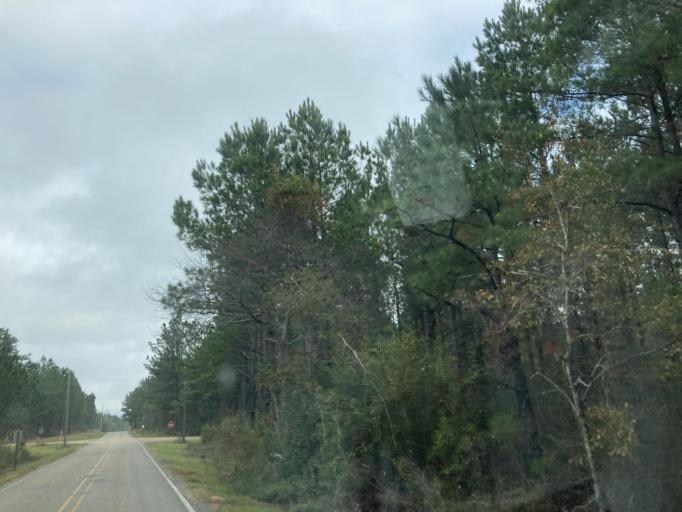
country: US
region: Mississippi
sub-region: Lamar County
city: Lumberton
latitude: 31.0225
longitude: -89.5701
